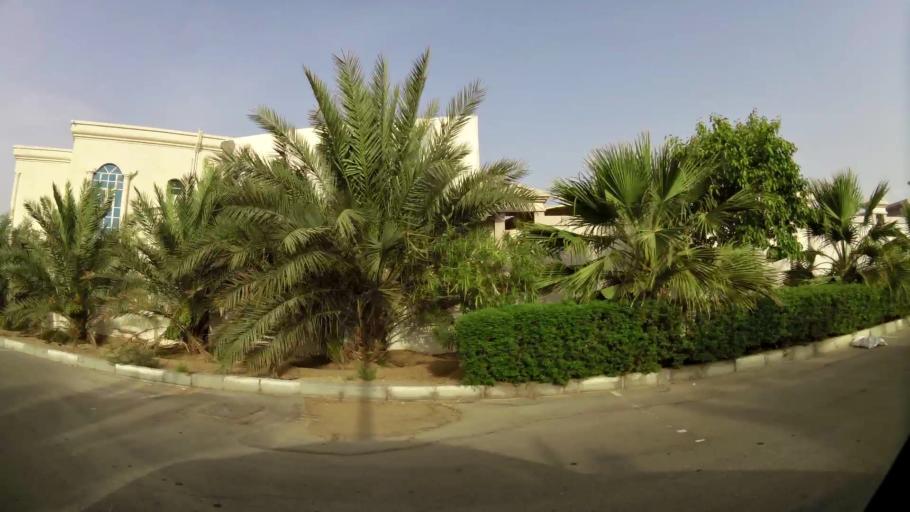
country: AE
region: Abu Dhabi
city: Al Ain
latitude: 24.1221
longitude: 55.7087
